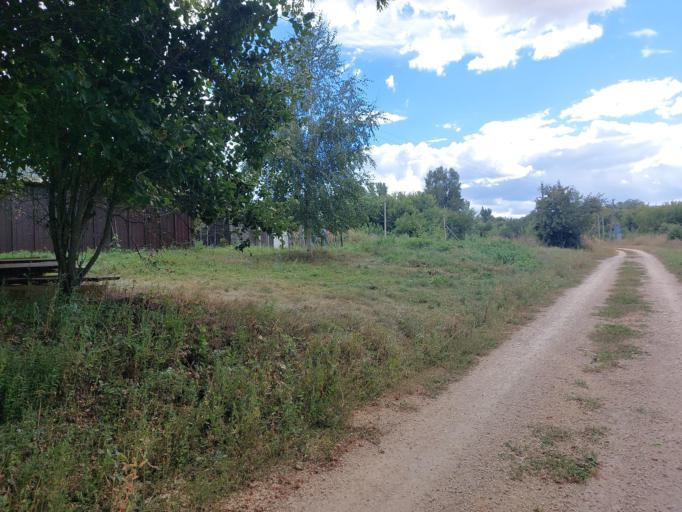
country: RU
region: Lipetsk
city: Terbuny
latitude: 52.2617
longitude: 38.2066
